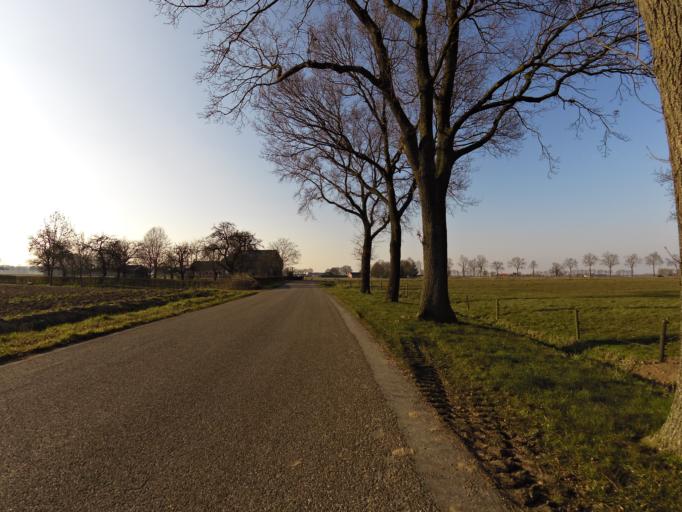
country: NL
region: Gelderland
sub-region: Gemeente Montferland
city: s-Heerenberg
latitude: 51.8948
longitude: 6.2891
